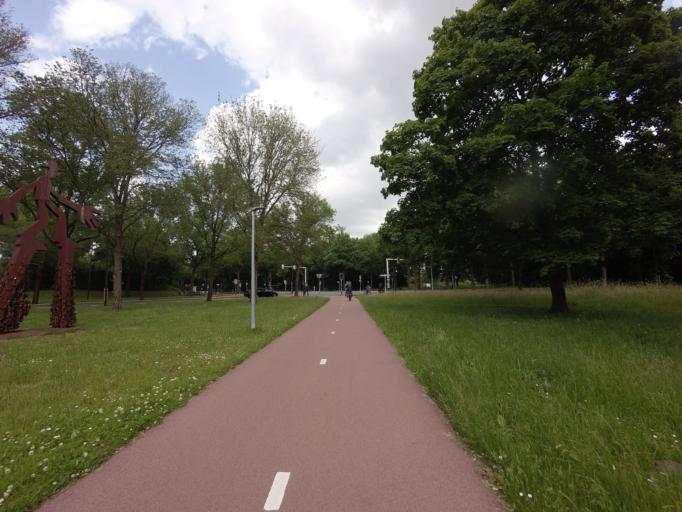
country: NL
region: North Holland
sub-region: Gemeente Huizen
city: Huizen
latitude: 52.2900
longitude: 5.2573
